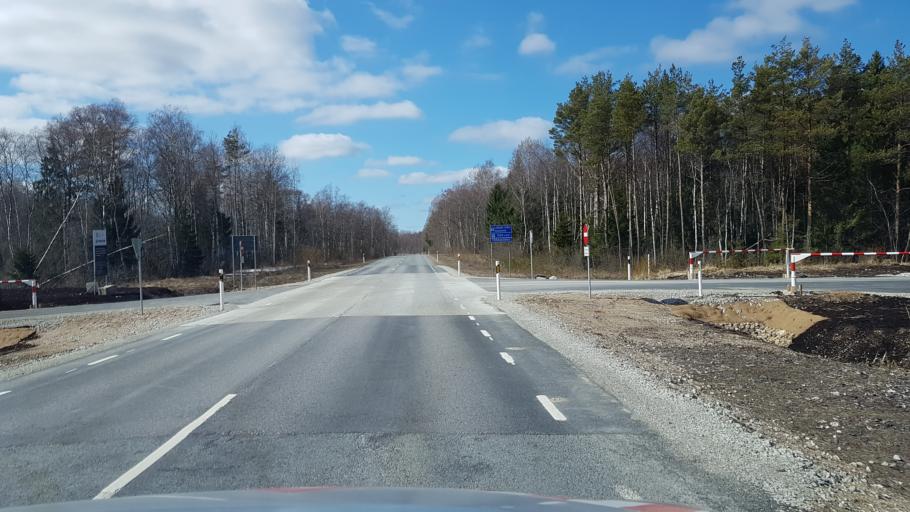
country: EE
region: Laeaene-Virumaa
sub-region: Tapa vald
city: Tapa
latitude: 59.2774
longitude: 25.8956
